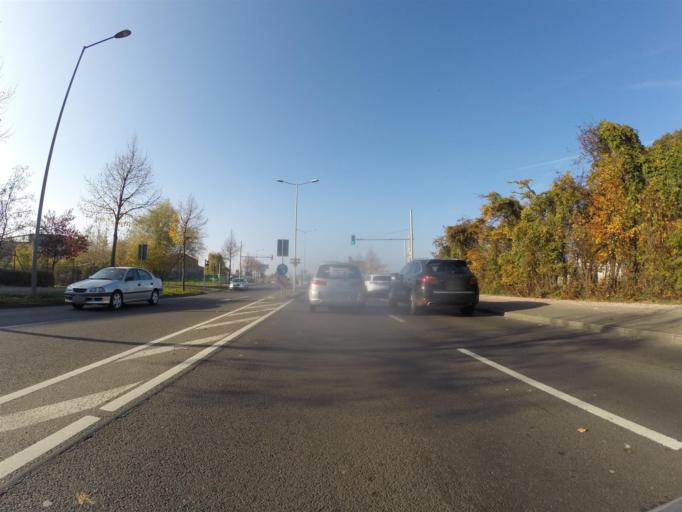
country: DE
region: Saxony
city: Leipzig
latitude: 51.3424
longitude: 12.3043
